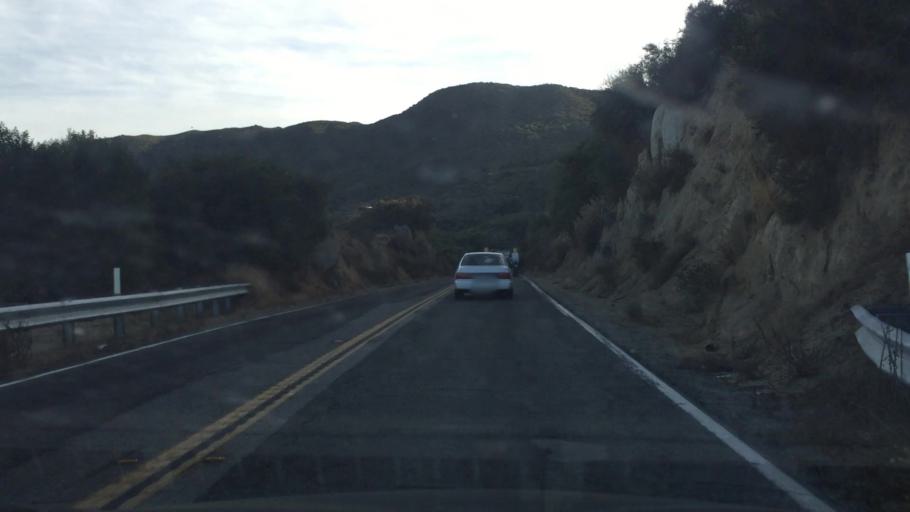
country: US
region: California
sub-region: Riverside County
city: Lakeland Village
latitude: 33.6538
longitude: -117.3957
